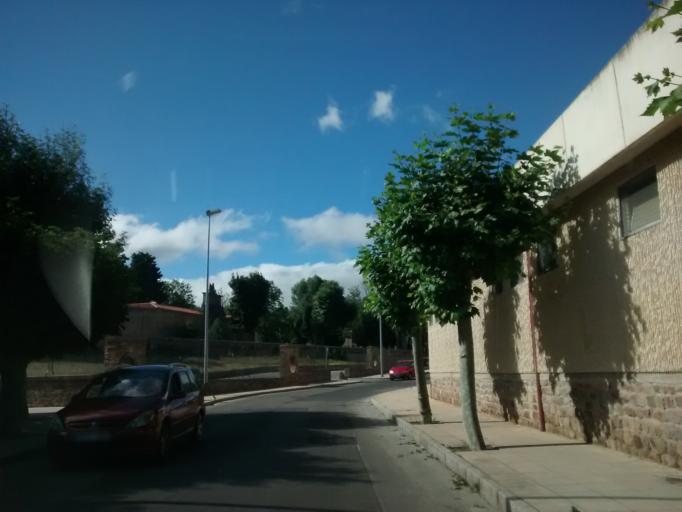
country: ES
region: Cantabria
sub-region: Provincia de Cantabria
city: Reinosa
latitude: 42.9993
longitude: -4.1422
